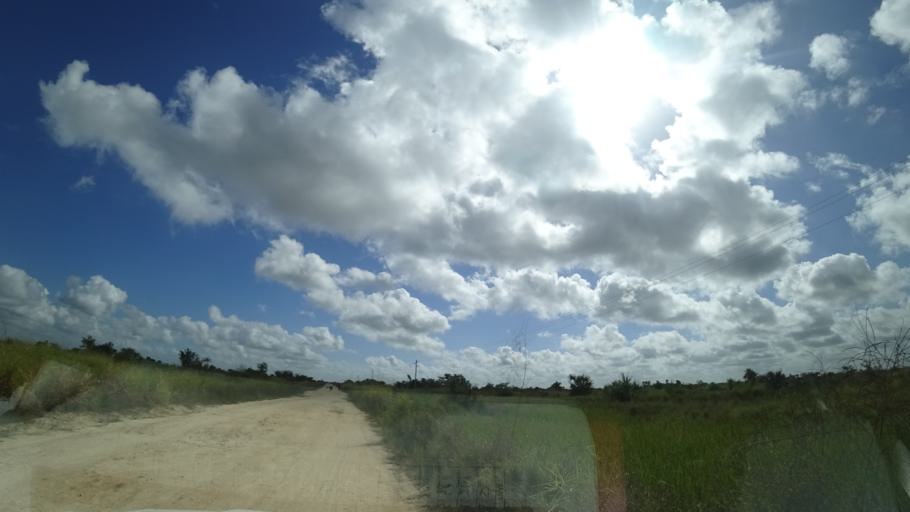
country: MZ
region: Sofala
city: Dondo
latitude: -19.4427
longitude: 34.5619
